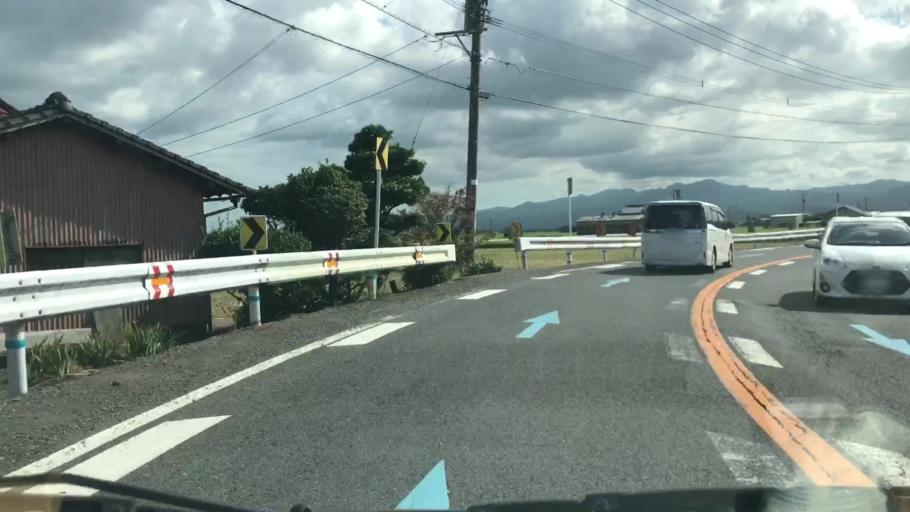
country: JP
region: Saga Prefecture
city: Kashima
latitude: 33.1631
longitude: 130.1682
